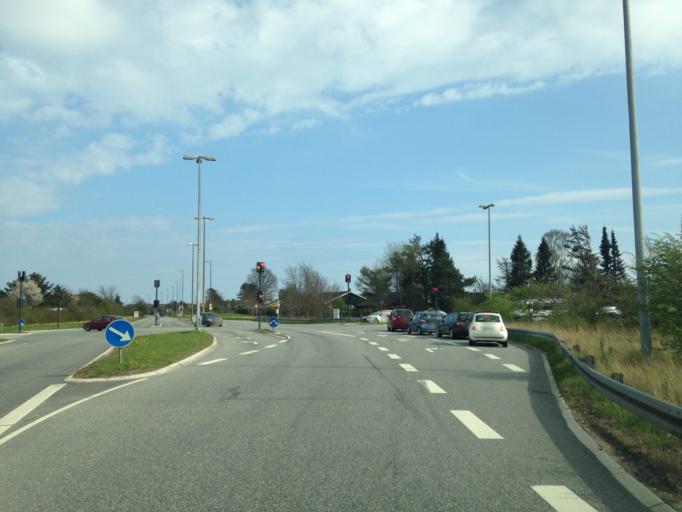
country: DK
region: Zealand
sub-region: Greve Kommune
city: Greve
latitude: 55.6007
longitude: 12.3078
